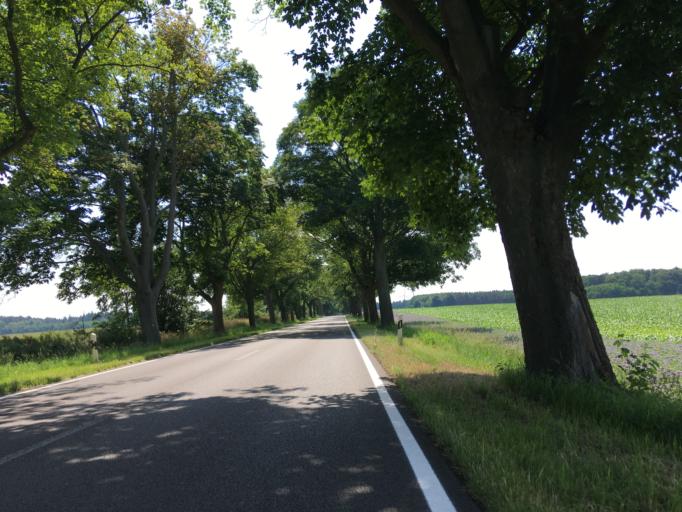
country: DE
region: Brandenburg
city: Werftpfuhl
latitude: 52.7310
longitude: 13.8377
